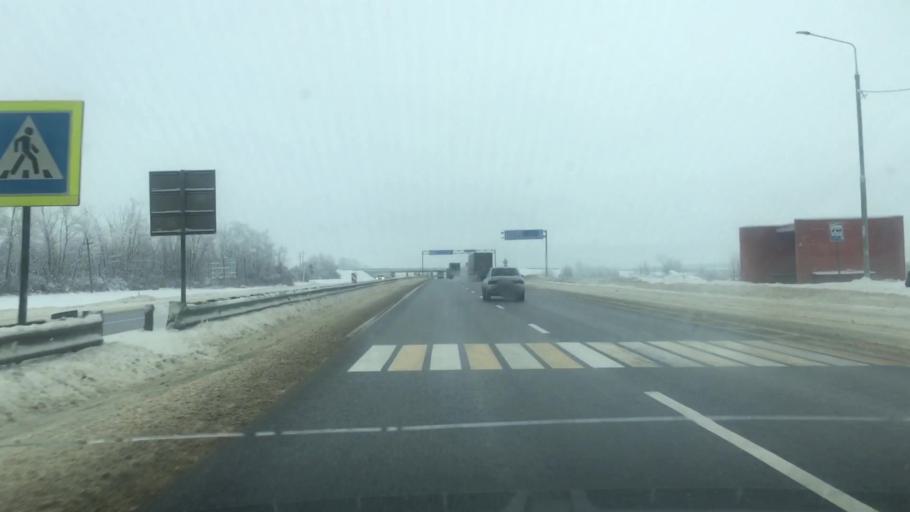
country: RU
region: Tula
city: Kazachka
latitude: 53.3042
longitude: 38.1784
